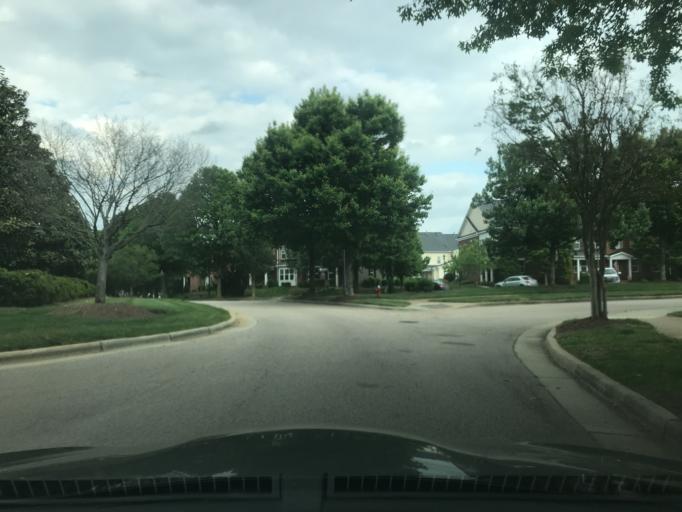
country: US
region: North Carolina
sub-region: Wake County
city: Wake Forest
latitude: 35.9301
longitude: -78.5644
